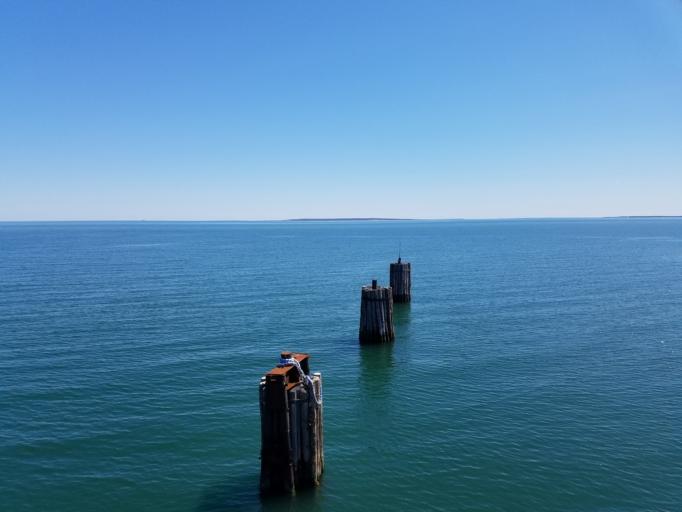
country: US
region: New York
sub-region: Suffolk County
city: Springs
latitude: 41.0119
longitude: -72.1689
